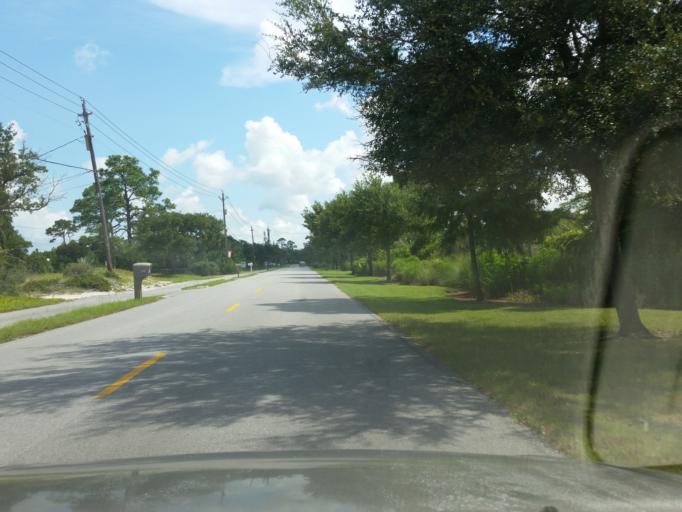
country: US
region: Alabama
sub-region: Baldwin County
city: Orange Beach
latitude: 30.3075
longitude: -87.4393
